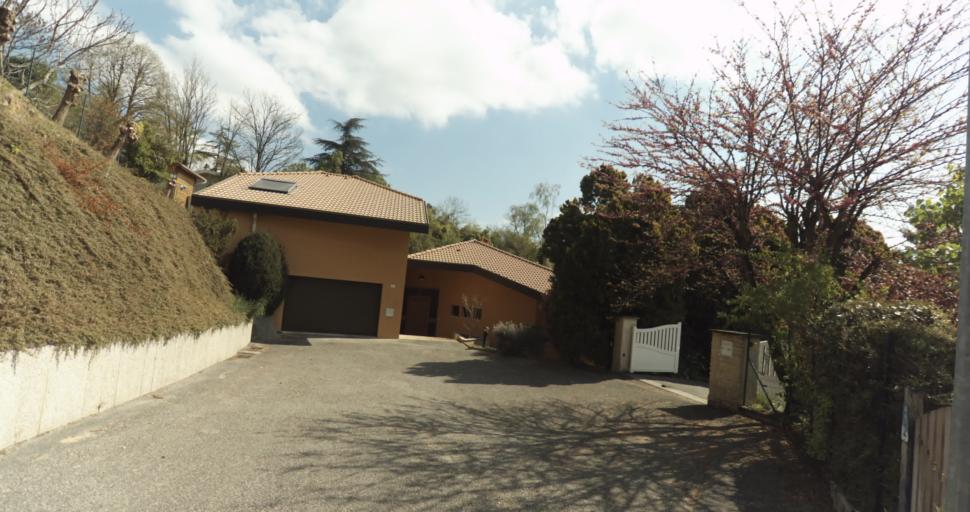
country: FR
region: Rhone-Alpes
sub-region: Departement de l'Isere
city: Saint-Marcellin
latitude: 45.1621
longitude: 5.3162
